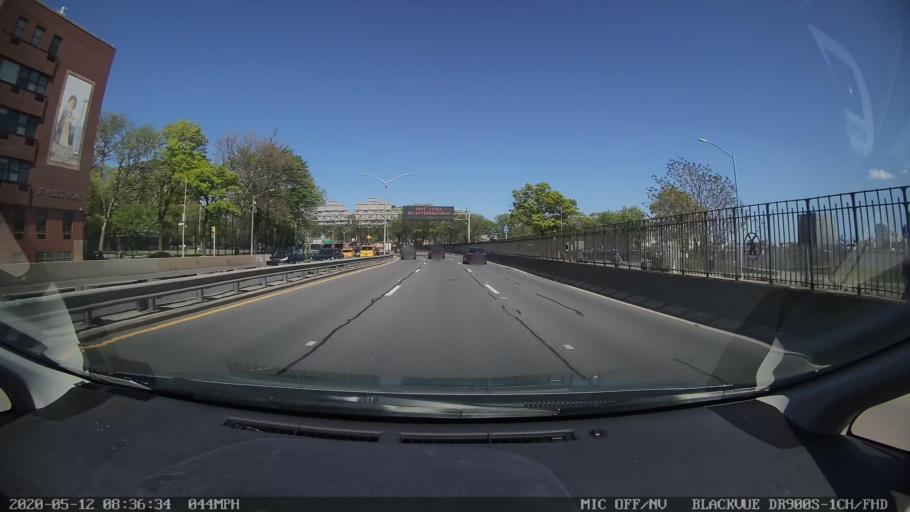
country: US
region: New York
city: New York City
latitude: 40.7119
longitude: -73.9801
